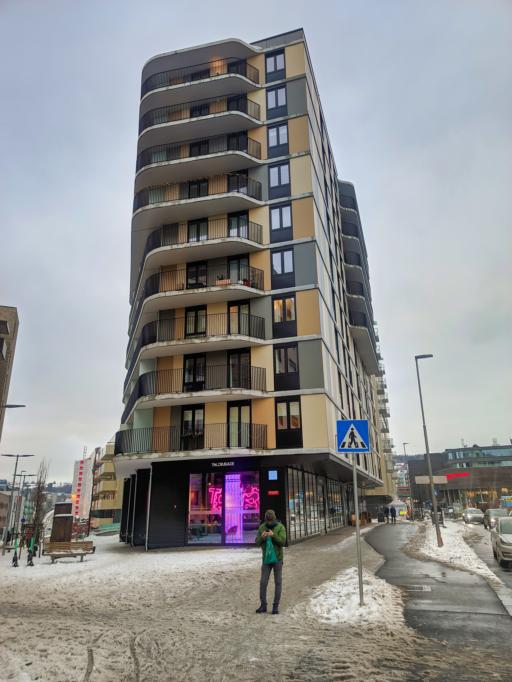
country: NO
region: Oslo
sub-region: Oslo
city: Oslo
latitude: 59.9454
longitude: 10.7722
